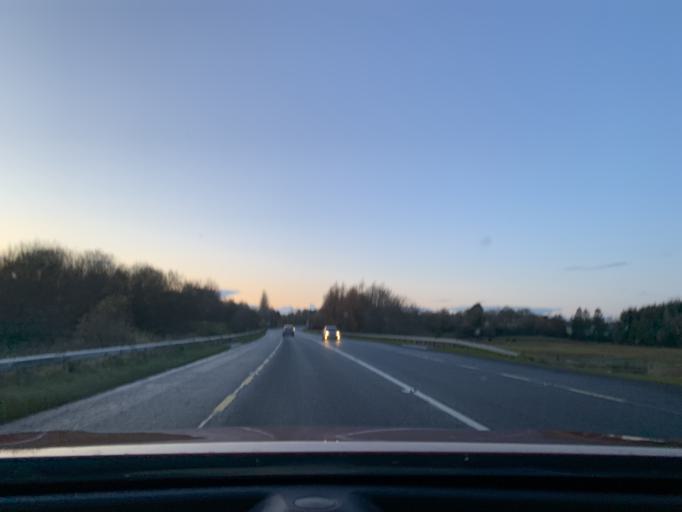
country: IE
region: Connaught
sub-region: County Leitrim
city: Carrick-on-Shannon
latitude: 53.9173
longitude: -7.9791
